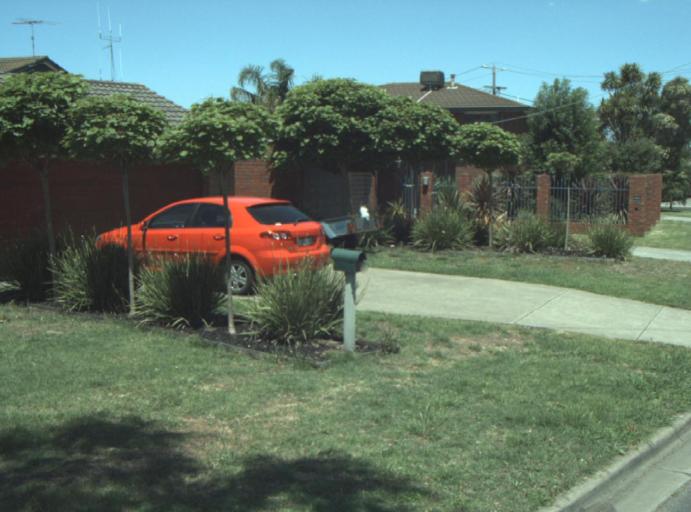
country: AU
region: Victoria
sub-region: Greater Geelong
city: Hamlyn Heights
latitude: -38.1151
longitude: 144.3225
